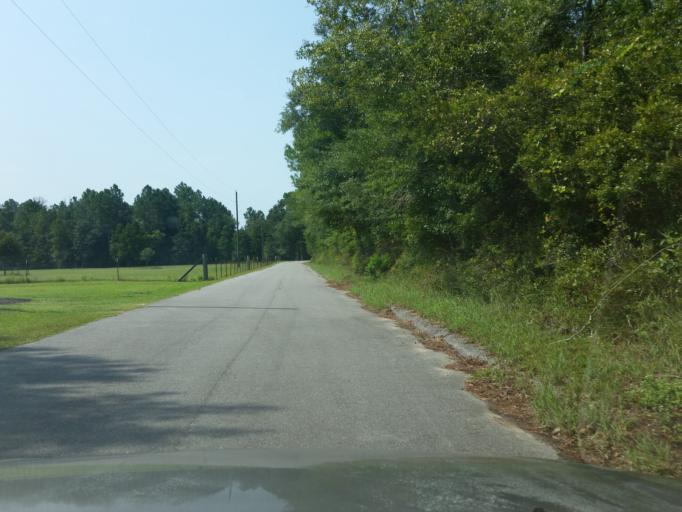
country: US
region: Florida
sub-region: Escambia County
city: Bellview
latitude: 30.4729
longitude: -87.3583
